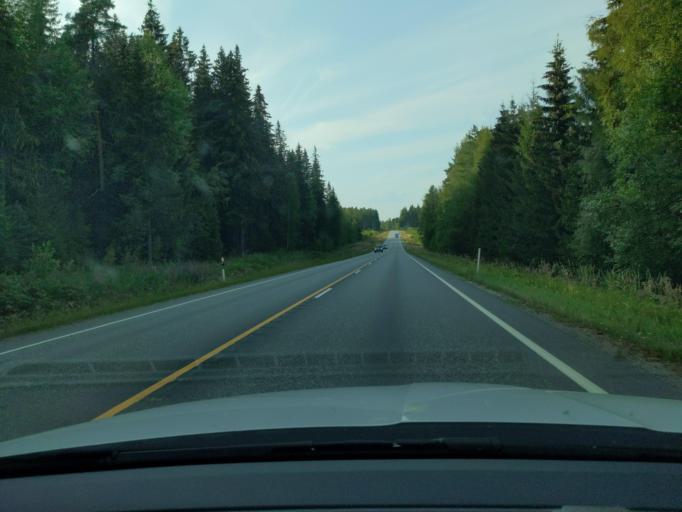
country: FI
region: Paijanne Tavastia
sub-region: Lahti
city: Padasjoki
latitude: 61.3277
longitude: 25.2736
